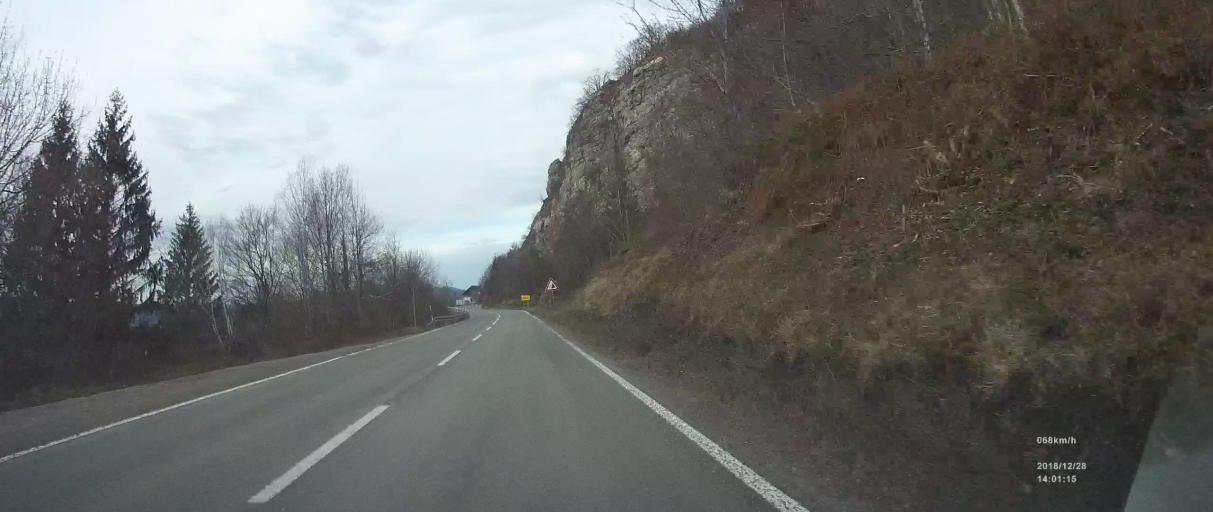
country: SI
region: Kostel
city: Kostel
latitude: 45.4185
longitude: 14.9090
